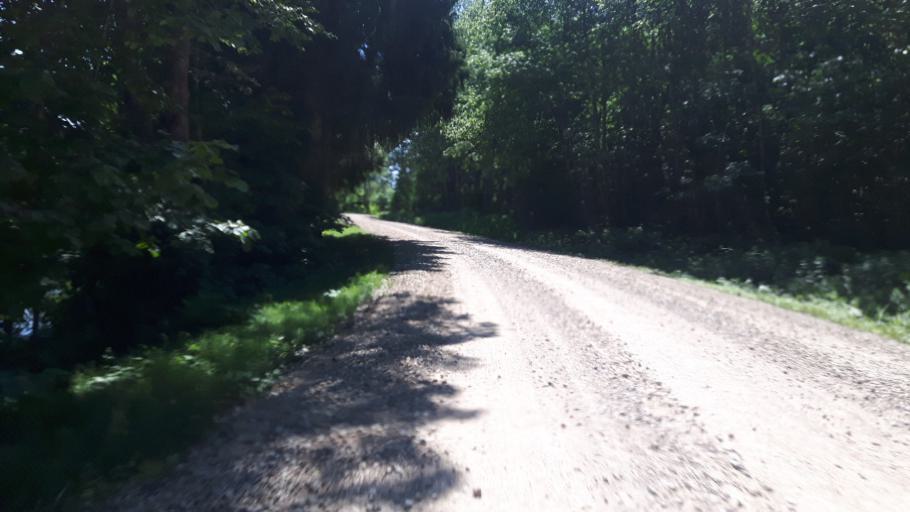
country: EE
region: Paernumaa
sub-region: Tootsi vald
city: Tootsi
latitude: 58.5048
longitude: 24.9061
